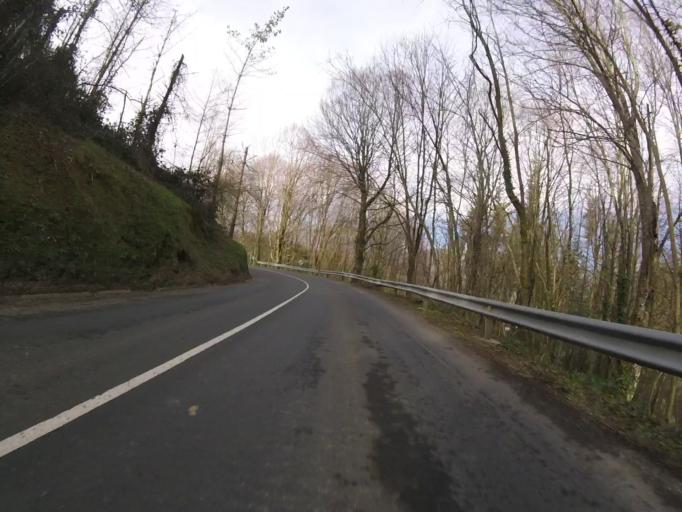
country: ES
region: Basque Country
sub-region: Provincia de Guipuzcoa
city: Beizama
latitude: 43.1654
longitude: -2.2187
